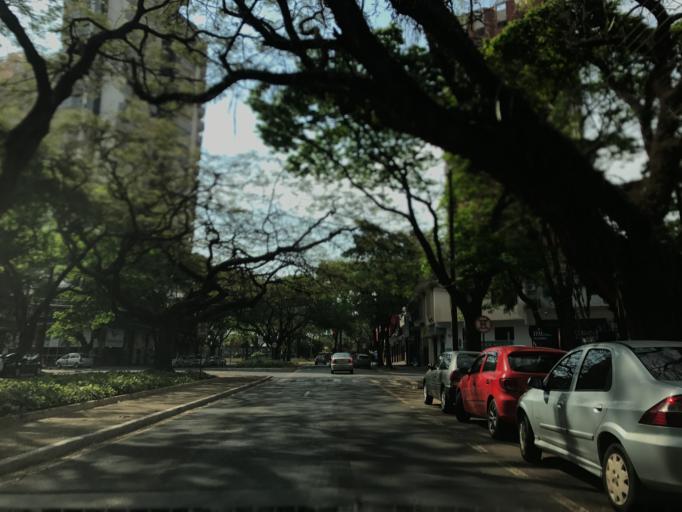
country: BR
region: Parana
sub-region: Maringa
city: Maringa
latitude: -23.4230
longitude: -51.9281
